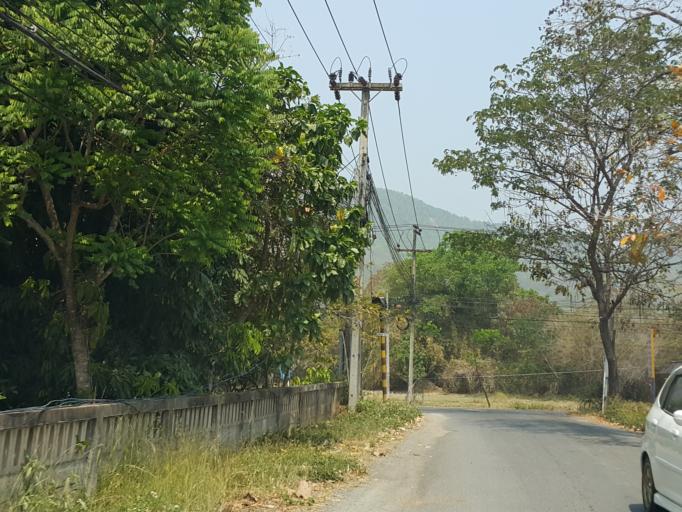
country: TH
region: Chiang Mai
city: Mae On
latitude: 18.7414
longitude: 99.2076
